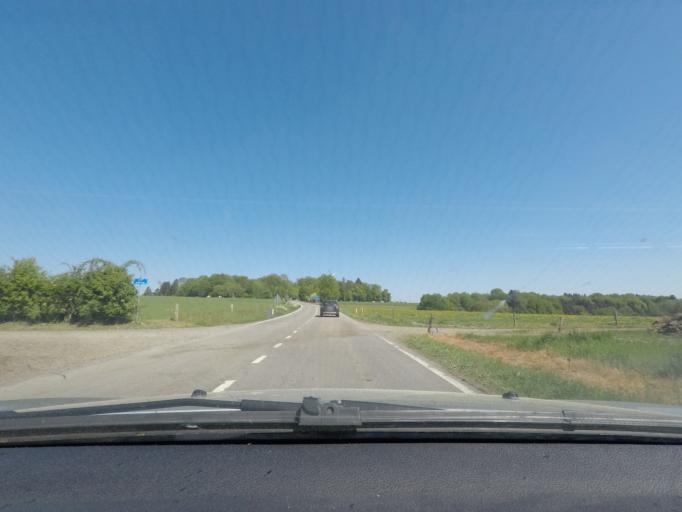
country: BE
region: Wallonia
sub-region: Province de Namur
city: Rochefort
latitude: 50.2138
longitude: 5.1482
